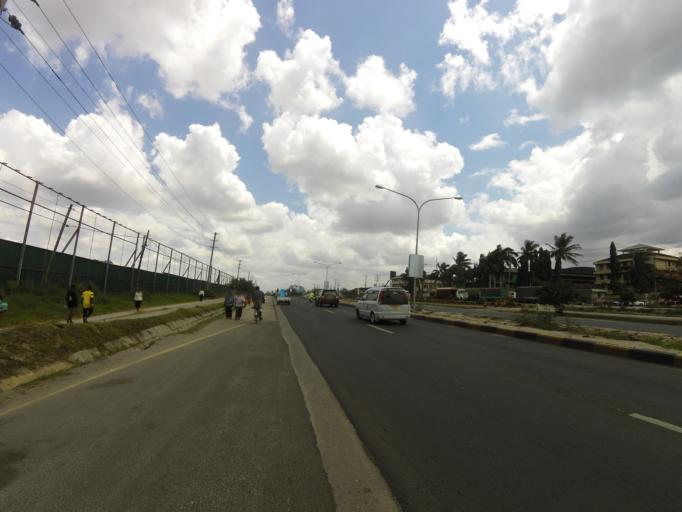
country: TZ
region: Dar es Salaam
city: Dar es Salaam
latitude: -6.8585
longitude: 39.2165
